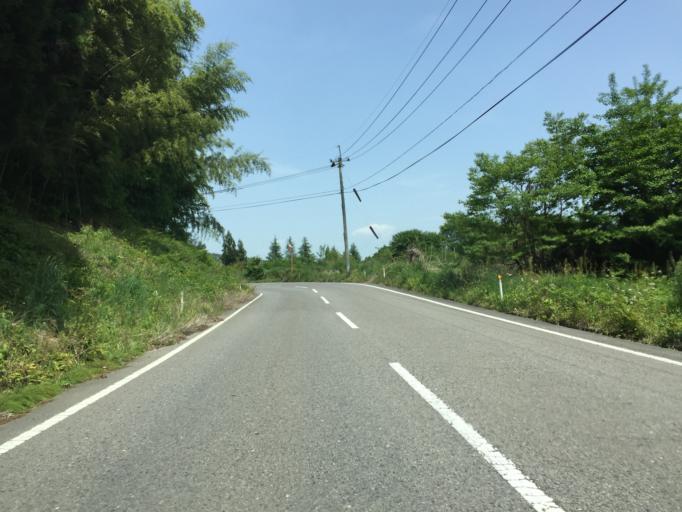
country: JP
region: Fukushima
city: Ishikawa
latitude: 37.1936
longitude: 140.4821
